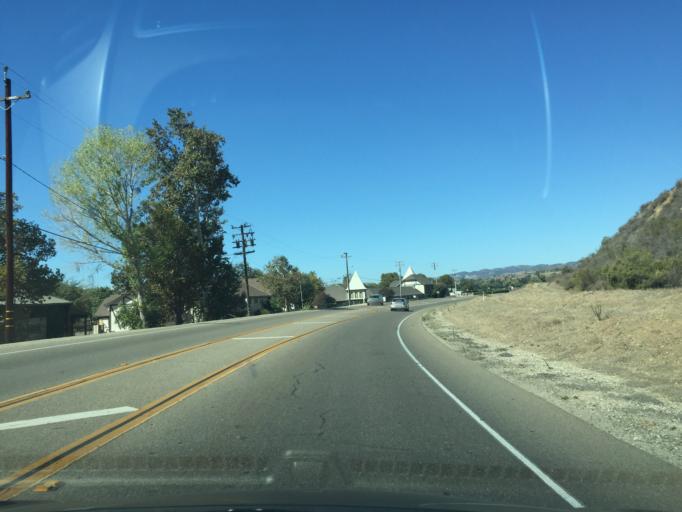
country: US
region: California
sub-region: Santa Barbara County
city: Solvang
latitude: 34.5943
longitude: -120.1524
